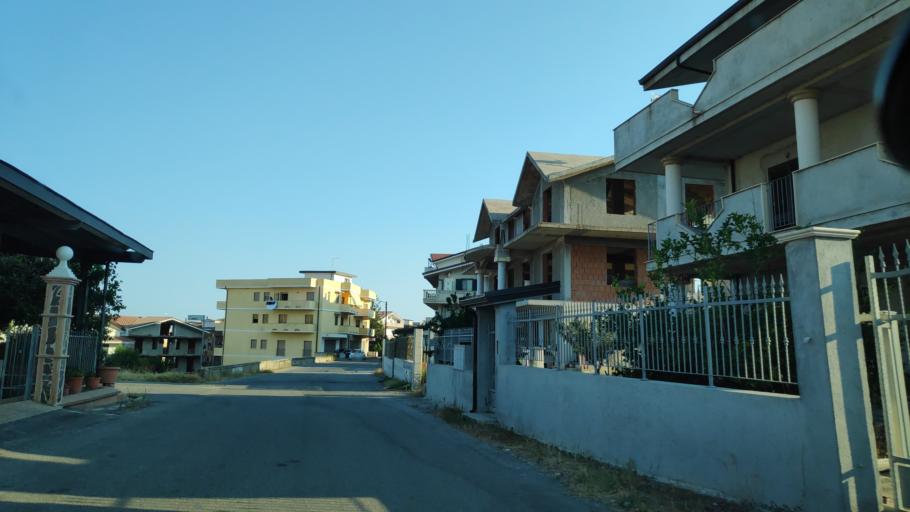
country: IT
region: Calabria
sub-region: Provincia di Reggio Calabria
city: Monasterace Marina
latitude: 38.4390
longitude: 16.5720
